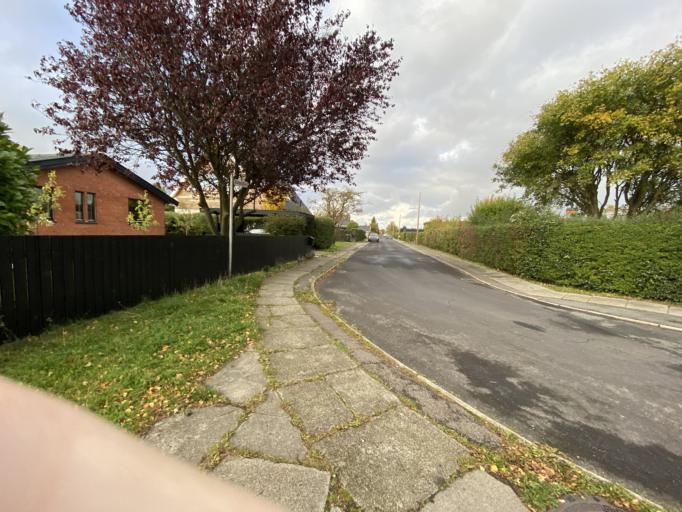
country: DK
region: Capital Region
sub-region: Dragor Kommune
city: Dragor
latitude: 55.5840
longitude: 12.6394
